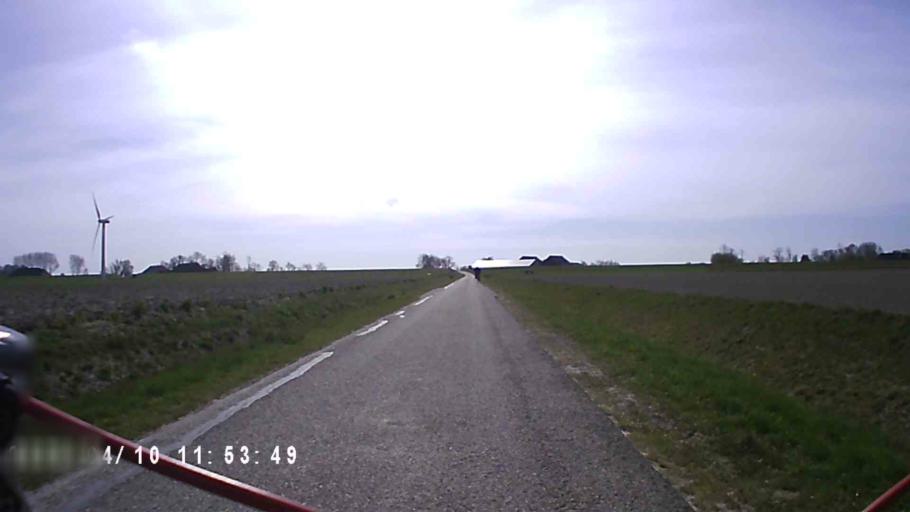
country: NL
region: Groningen
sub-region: Gemeente De Marne
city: Ulrum
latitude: 53.3907
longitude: 6.3312
